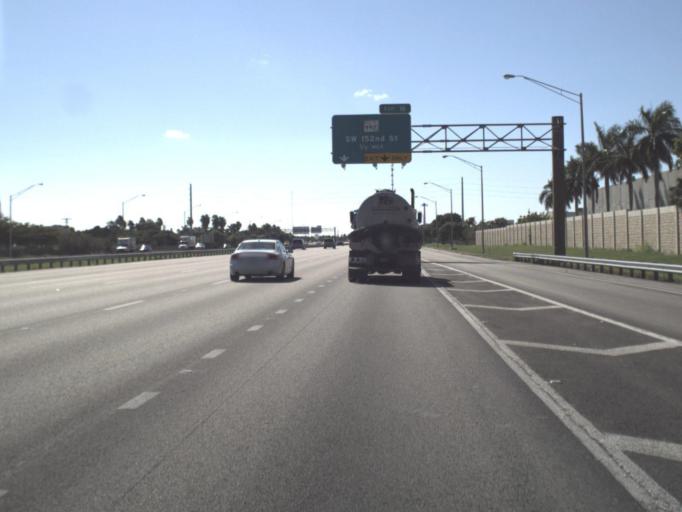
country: US
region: Florida
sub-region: Miami-Dade County
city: Three Lakes
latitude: 25.6418
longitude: -80.3858
